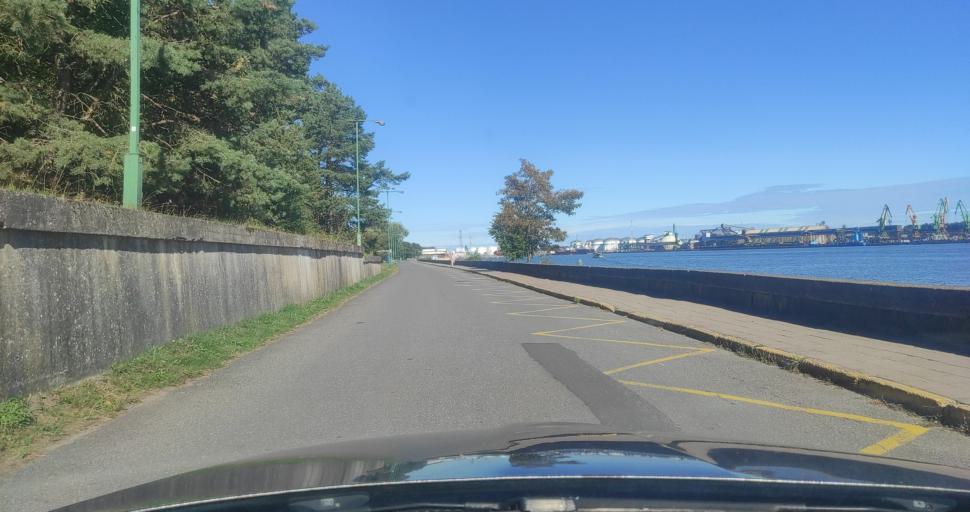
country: LT
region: Klaipedos apskritis
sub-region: Klaipeda
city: Klaipeda
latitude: 55.7104
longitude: 21.1092
